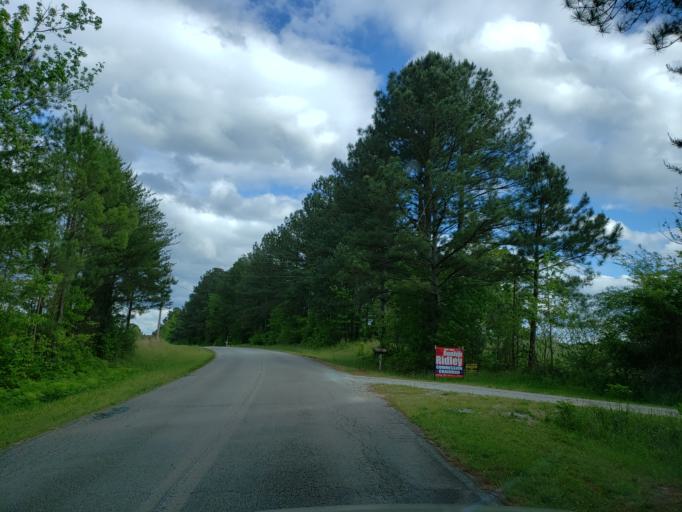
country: US
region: Georgia
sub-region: Haralson County
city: Tallapoosa
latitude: 33.7976
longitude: -85.3546
